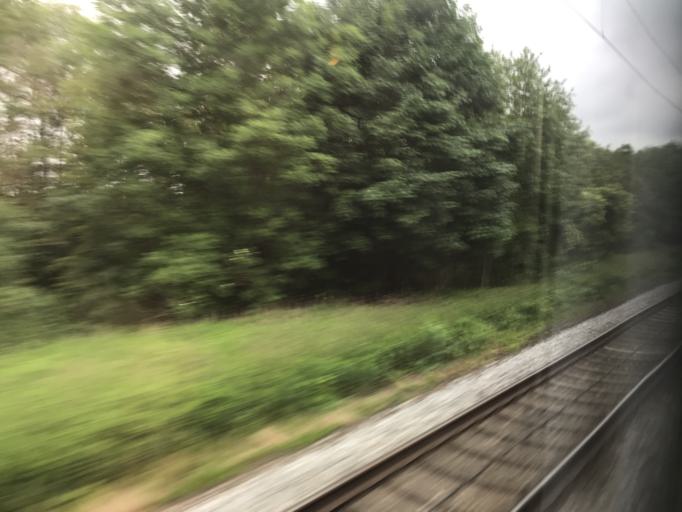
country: DE
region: Bavaria
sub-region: Upper Bavaria
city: Grobenzell
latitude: 48.2057
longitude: 11.3523
